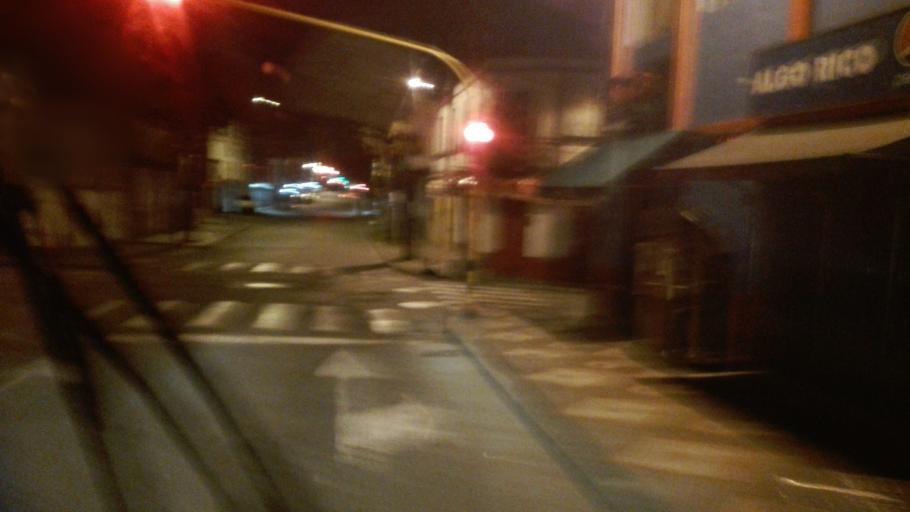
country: CO
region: Risaralda
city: Pereira
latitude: 4.8177
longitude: -75.6971
